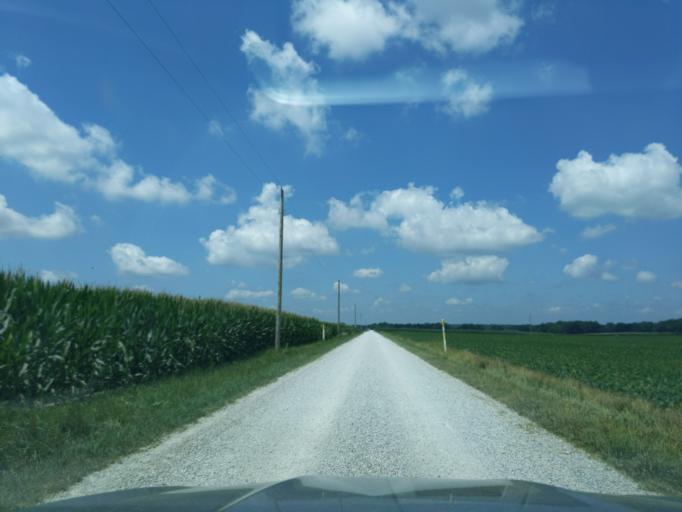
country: US
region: Indiana
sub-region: Ripley County
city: Osgood
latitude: 39.2207
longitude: -85.3721
